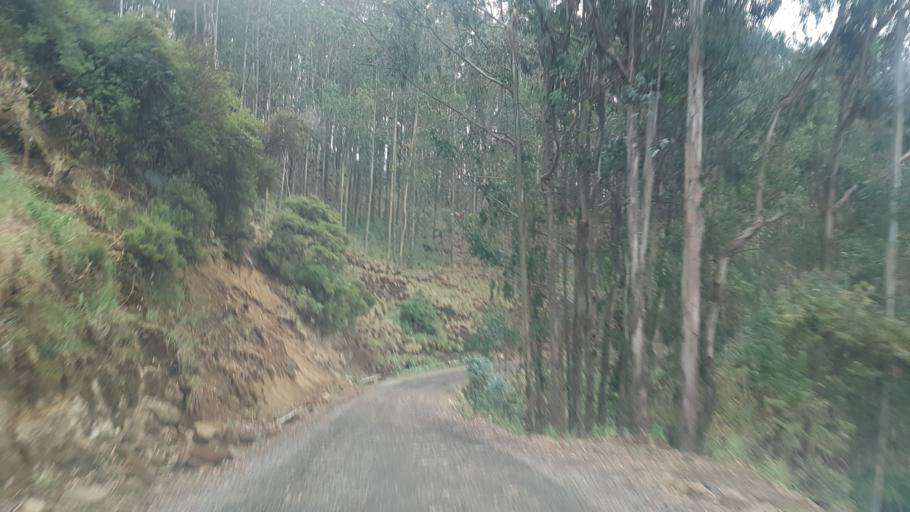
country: ET
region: Amhara
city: Finote Selam
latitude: 10.7852
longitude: 37.6682
